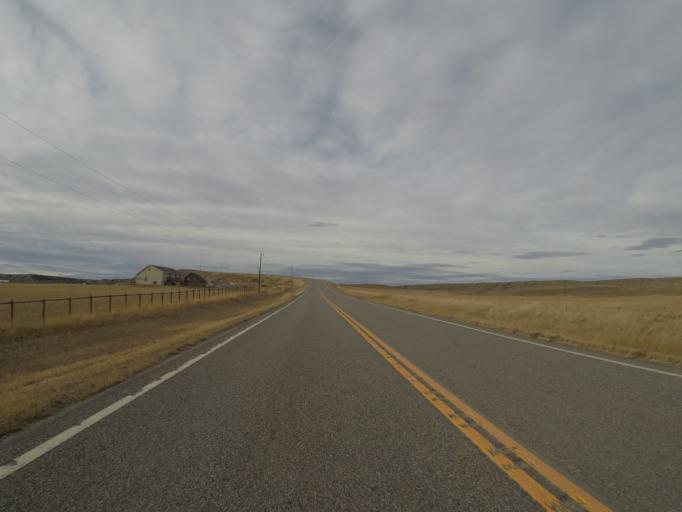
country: US
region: Montana
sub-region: Yellowstone County
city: Laurel
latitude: 45.8437
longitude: -108.7264
